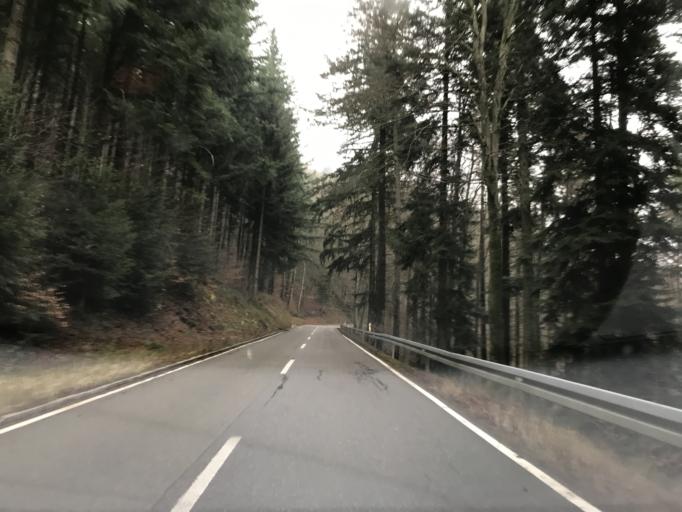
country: DE
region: Baden-Wuerttemberg
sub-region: Freiburg Region
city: Wehr
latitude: 47.6163
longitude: 7.9344
